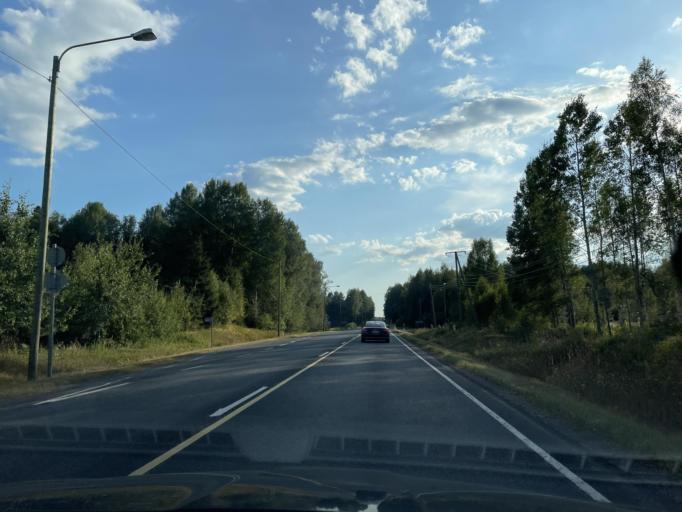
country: FI
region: Haeme
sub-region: Haemeenlinna
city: Tuulos
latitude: 61.0951
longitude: 24.8122
